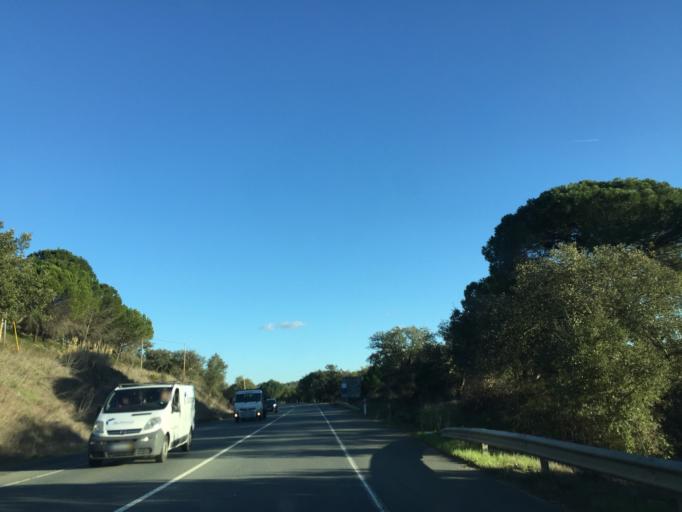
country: PT
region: Setubal
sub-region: Grandola
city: Grandola
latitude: 38.1237
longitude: -8.4545
